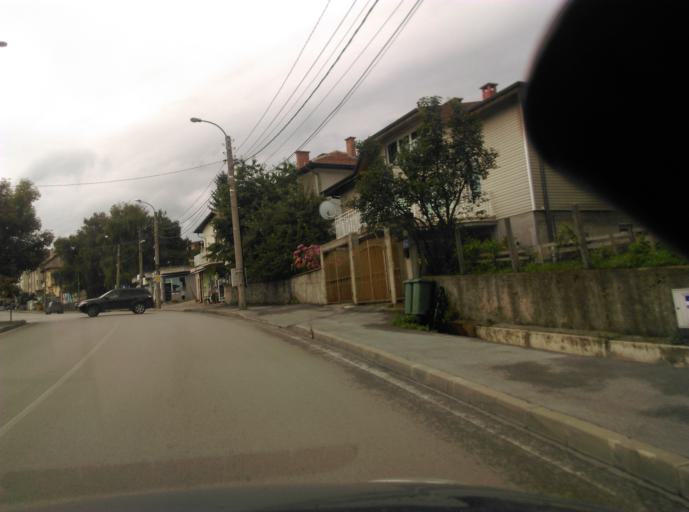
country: BG
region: Sofia-Capital
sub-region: Stolichna Obshtina
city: Sofia
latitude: 42.6312
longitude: 23.3059
